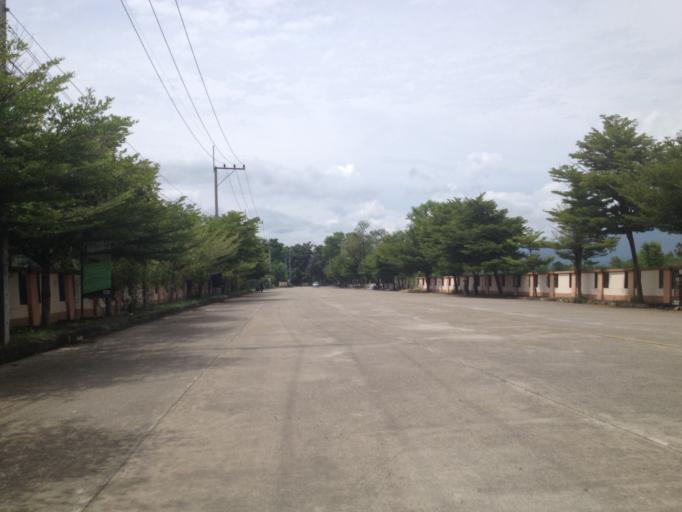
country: TH
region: Chiang Mai
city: Hang Dong
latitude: 18.7029
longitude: 98.9398
